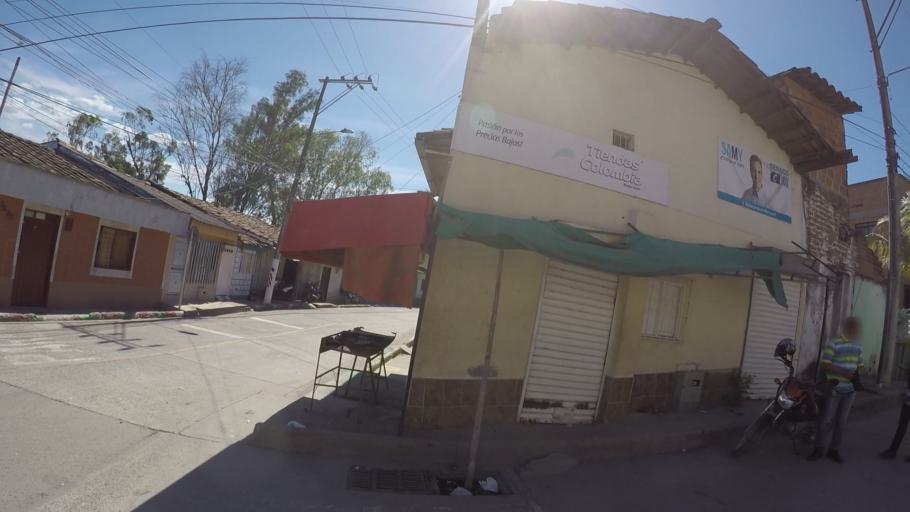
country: CO
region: Valle del Cauca
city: Cartago
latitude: 4.7592
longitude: -75.9010
